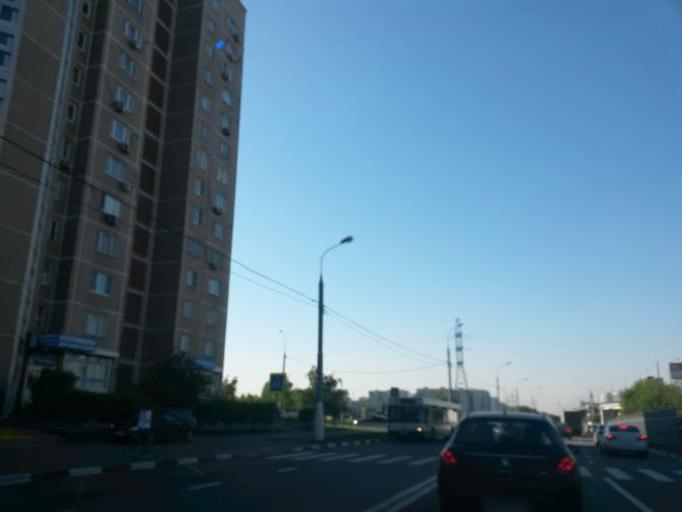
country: RU
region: Moscow
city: Brateyevo
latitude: 55.6360
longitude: 37.7484
